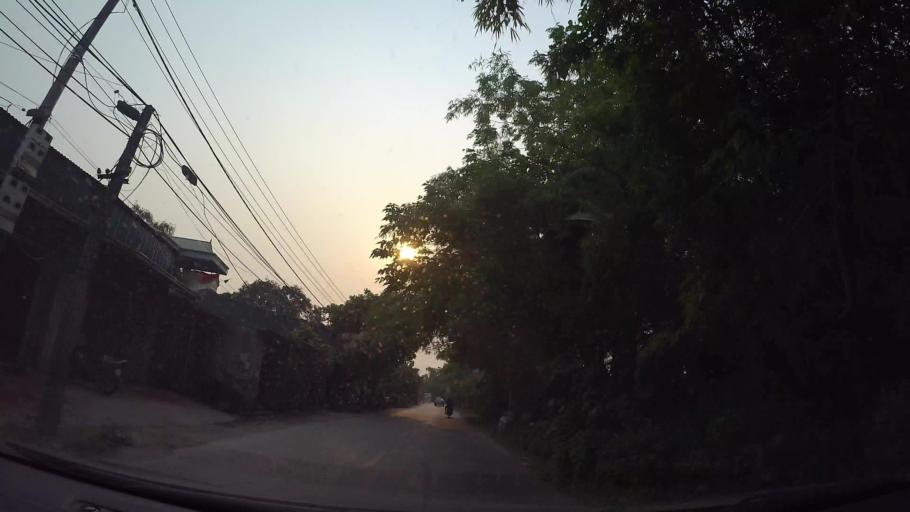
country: VN
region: Ha Noi
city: Thuong Tin
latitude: 20.8699
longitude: 105.8196
